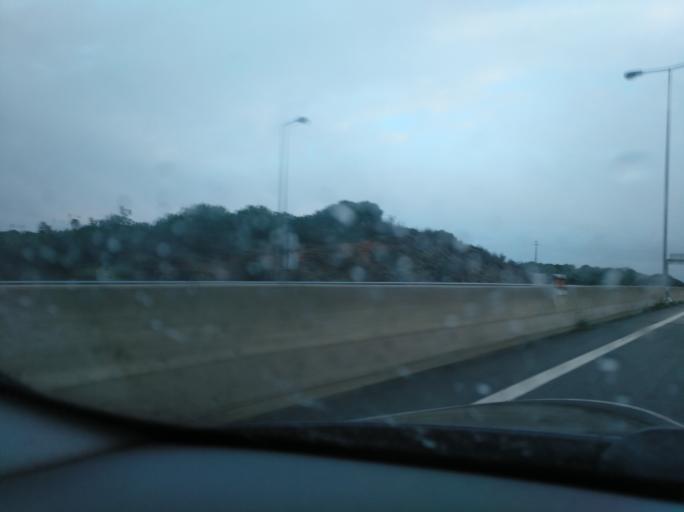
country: PT
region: Faro
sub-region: Castro Marim
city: Castro Marim
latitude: 37.2917
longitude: -7.4870
